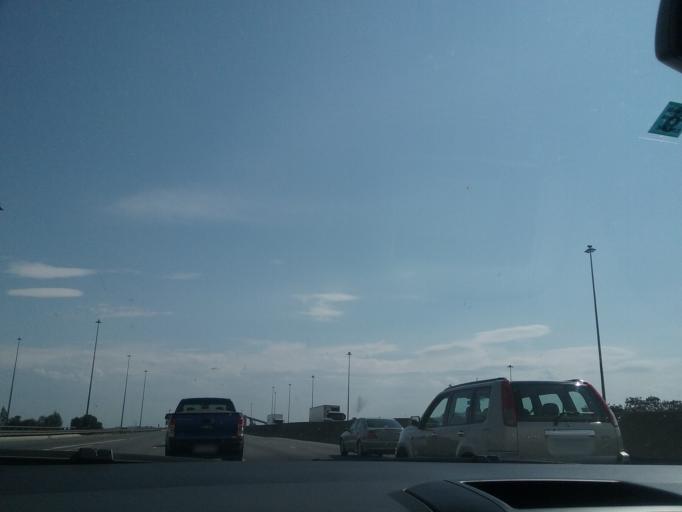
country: ZA
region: Gauteng
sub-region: Ekurhuleni Metropolitan Municipality
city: Germiston
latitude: -26.2120
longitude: 28.1348
